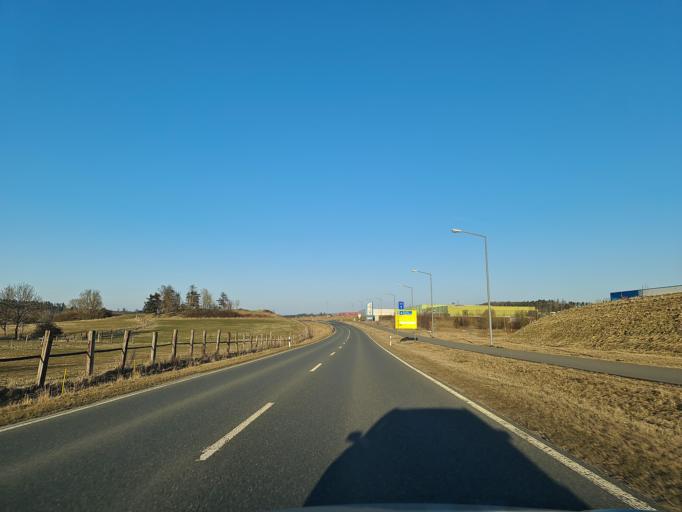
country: DE
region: Bavaria
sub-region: Upper Franconia
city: Trogen
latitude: 50.3389
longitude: 11.9503
